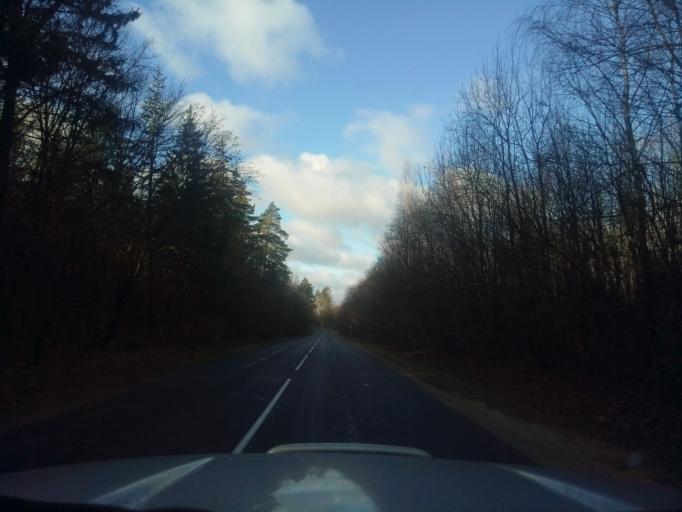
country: BY
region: Minsk
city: Kapyl'
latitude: 53.1753
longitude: 27.0122
